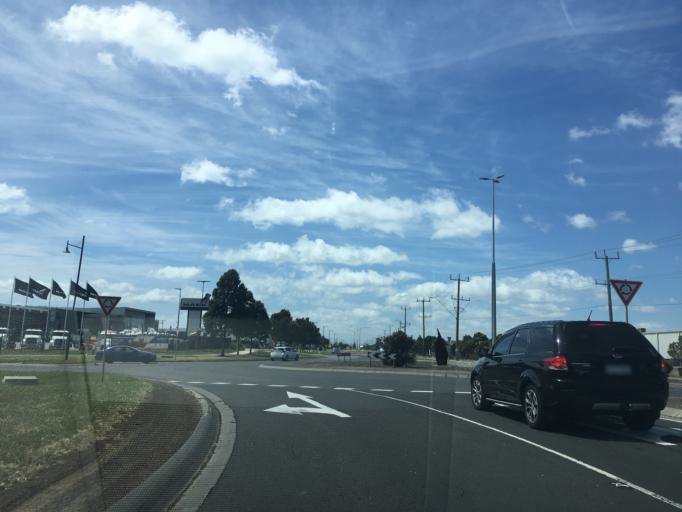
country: AU
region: Victoria
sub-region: Wyndham
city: Truganina
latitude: -37.8117
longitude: 144.7654
